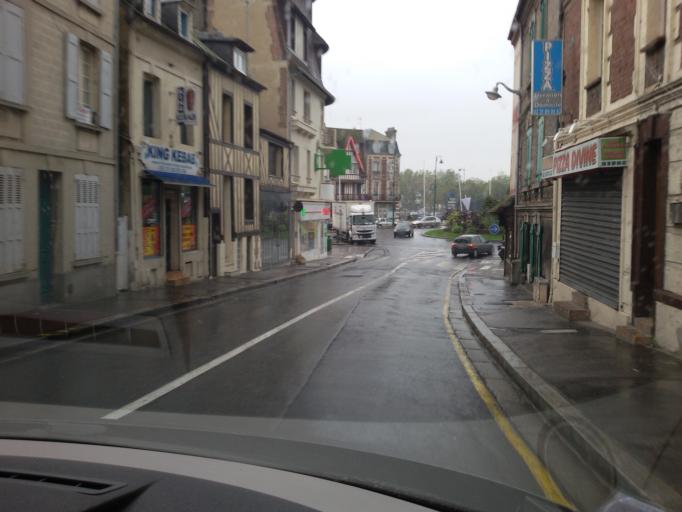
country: FR
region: Lower Normandy
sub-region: Departement du Calvados
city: Trouville-sur-Mer
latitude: 49.3621
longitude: 0.0865
